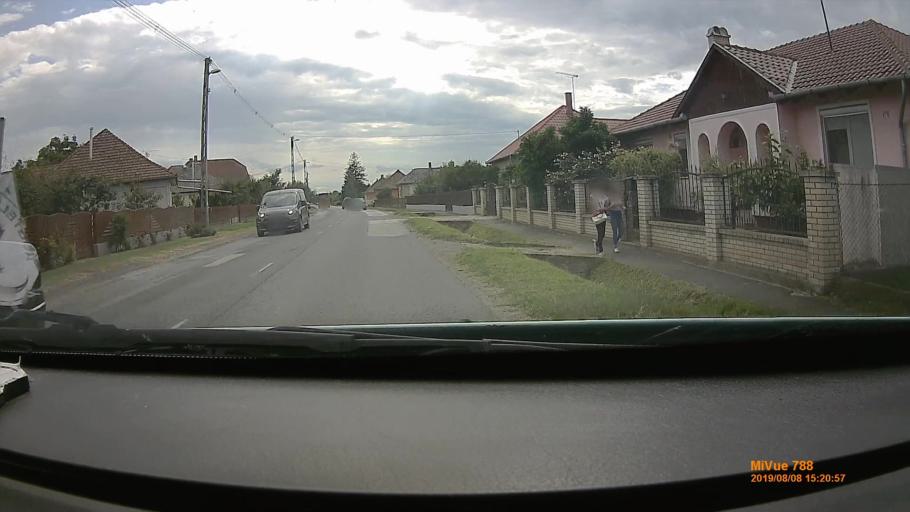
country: HU
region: Szabolcs-Szatmar-Bereg
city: Tunyogmatolcs
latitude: 47.9687
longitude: 22.4514
